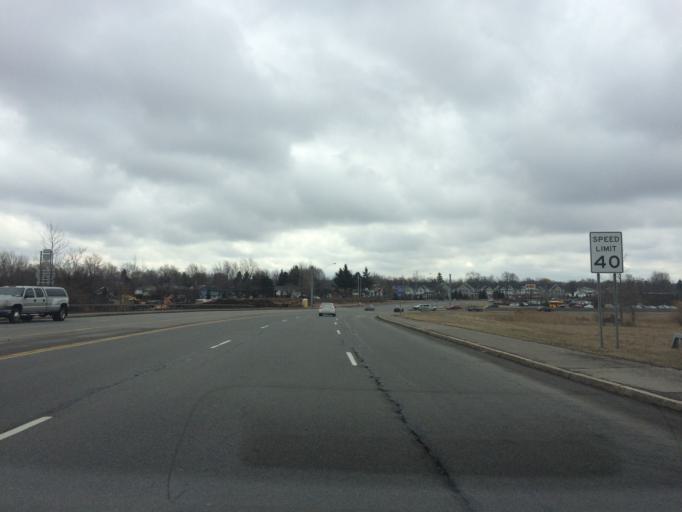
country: US
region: New York
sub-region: Monroe County
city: Rochester
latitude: 43.0756
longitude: -77.6264
